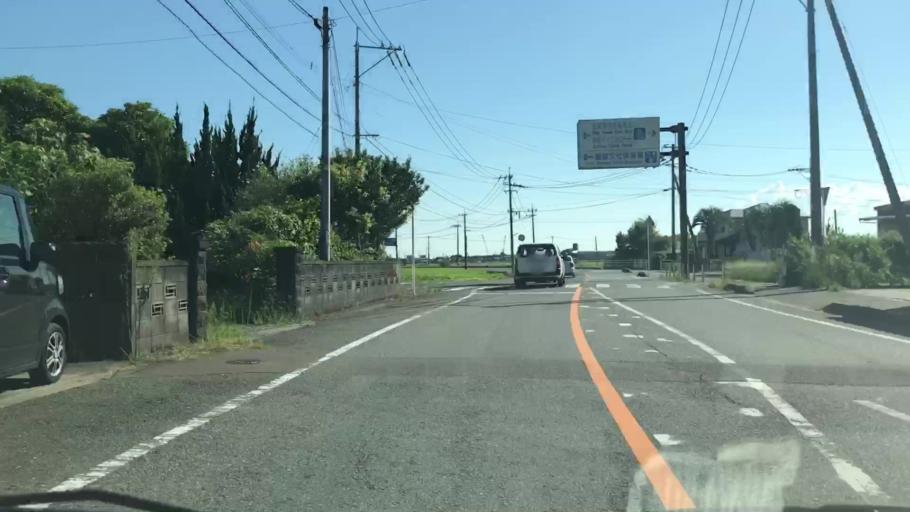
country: JP
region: Saga Prefecture
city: Okawa
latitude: 33.2230
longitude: 130.3515
